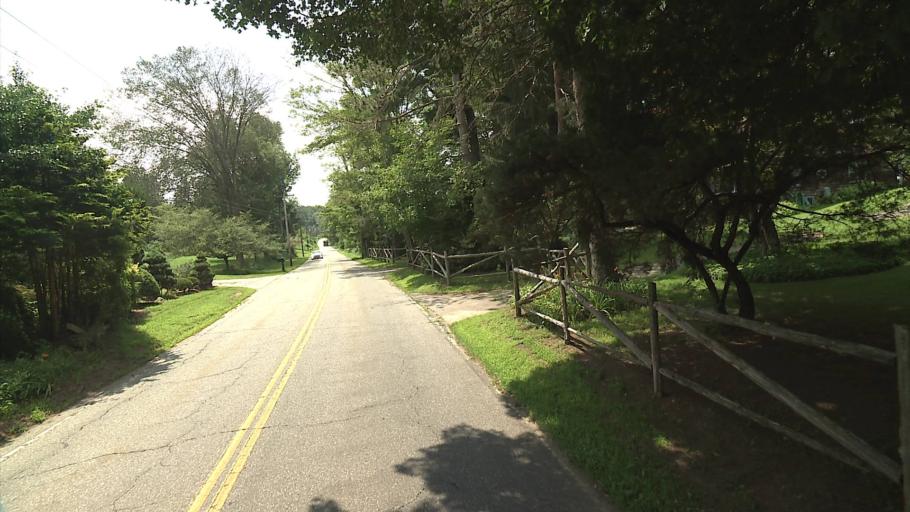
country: US
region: Connecticut
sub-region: New London County
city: Baltic
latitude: 41.5962
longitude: -72.1271
